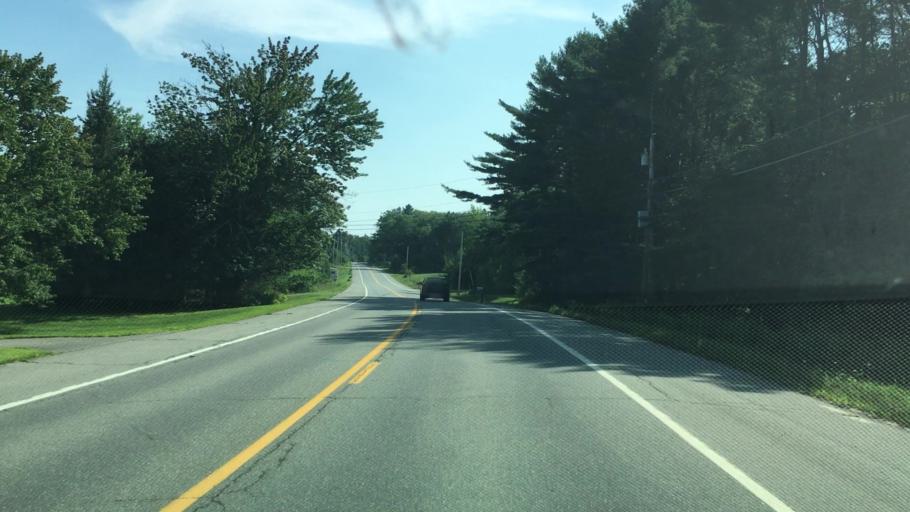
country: US
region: Maine
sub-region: Waldo County
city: Winterport
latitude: 44.6523
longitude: -68.8388
